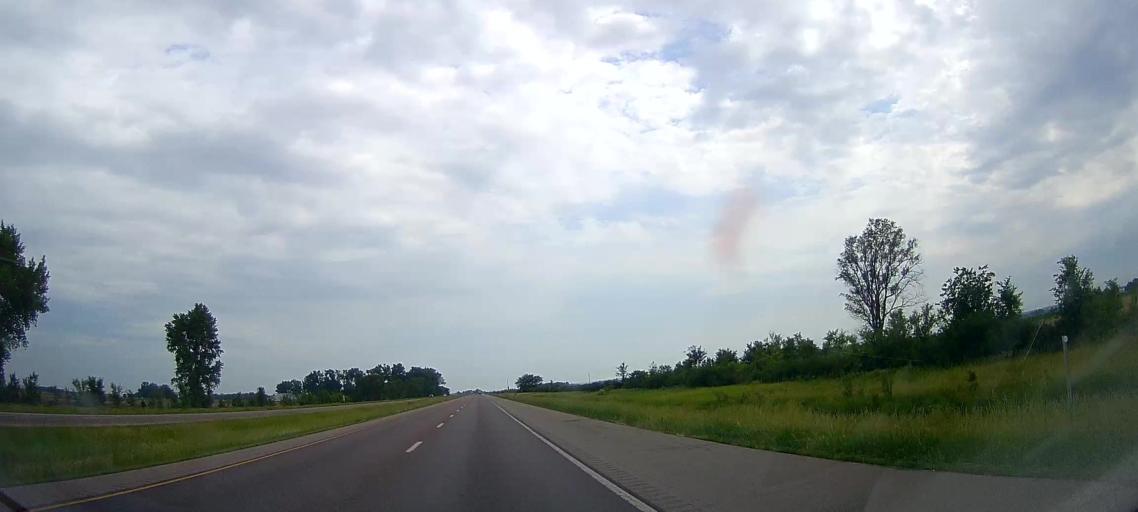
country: US
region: Nebraska
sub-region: Thurston County
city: Macy
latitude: 42.2065
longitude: -96.2416
